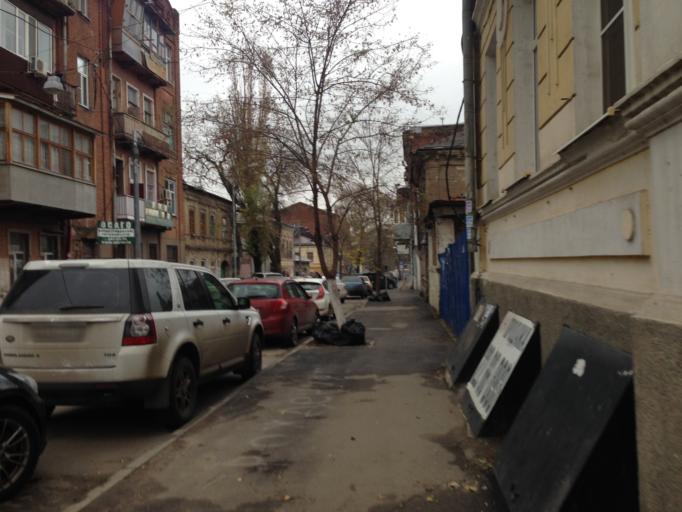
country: RU
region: Rostov
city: Rostov-na-Donu
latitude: 47.2174
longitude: 39.7192
